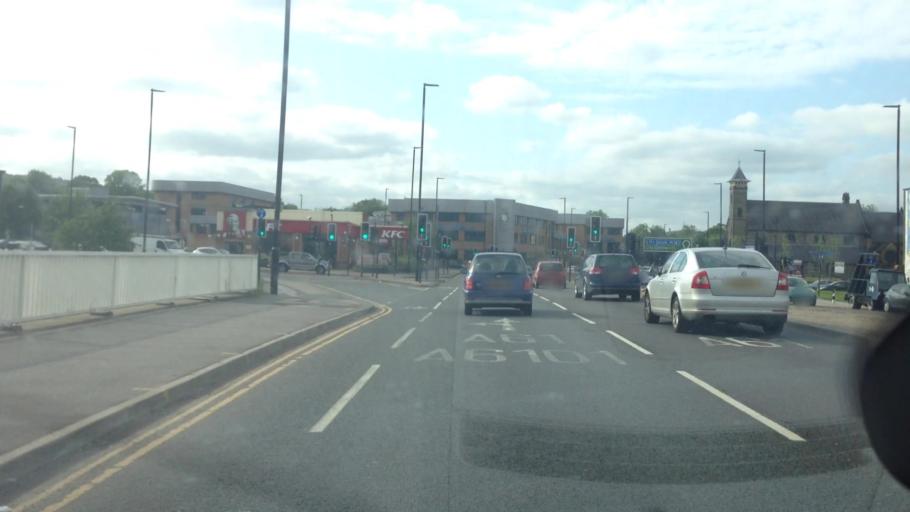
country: GB
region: England
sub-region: Sheffield
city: Sheffield
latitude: 53.4037
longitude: -1.4946
